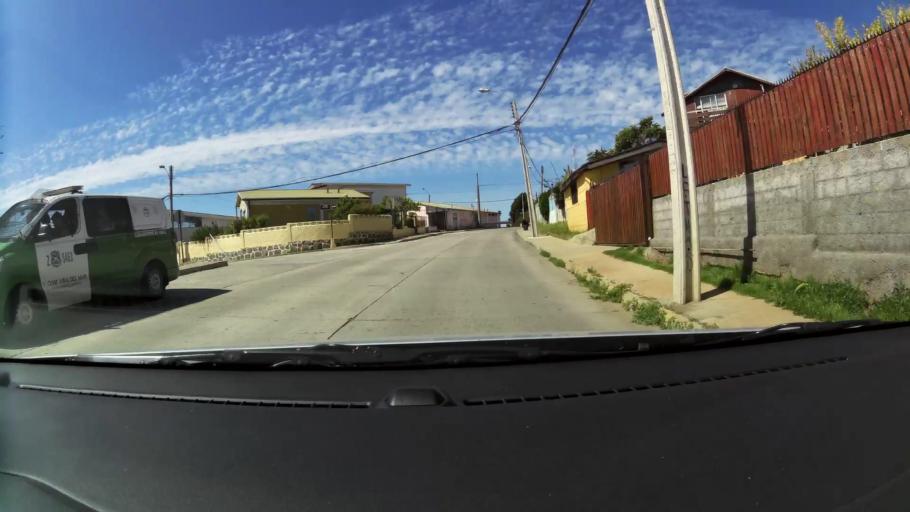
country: CL
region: Valparaiso
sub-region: Provincia de Valparaiso
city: Vina del Mar
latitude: -33.0417
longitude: -71.5734
